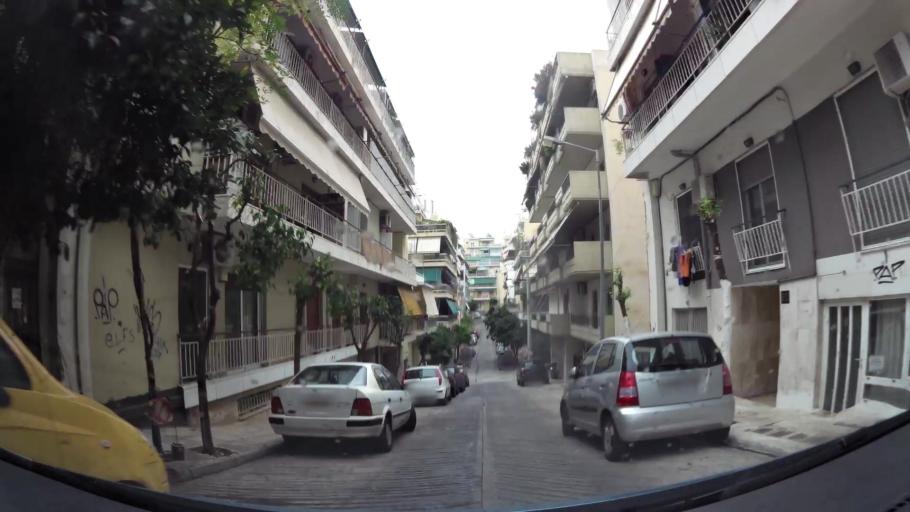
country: GR
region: Attica
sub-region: Nomarchia Athinas
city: Vyronas
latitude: 37.9616
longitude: 23.7496
